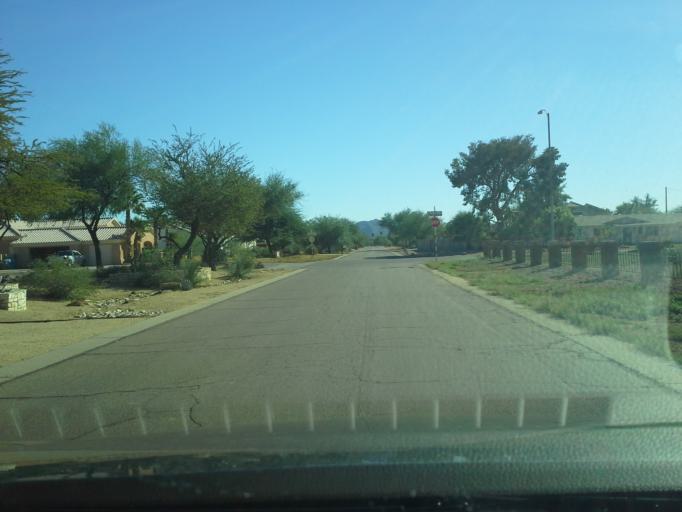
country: US
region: Arizona
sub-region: Maricopa County
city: Paradise Valley
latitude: 33.6340
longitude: -111.9920
